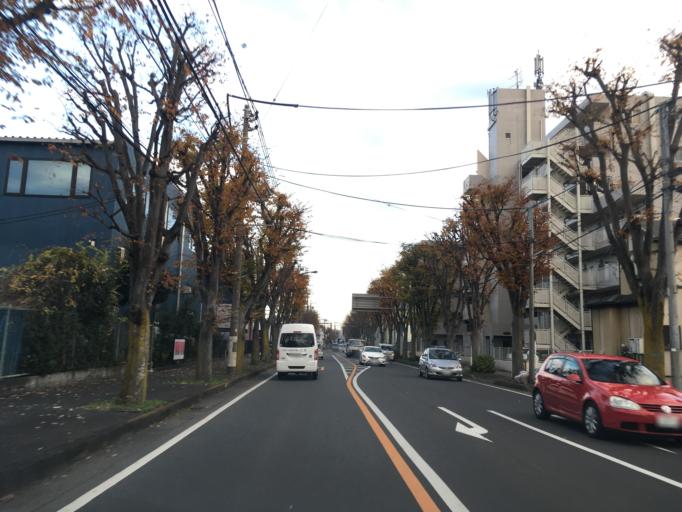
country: JP
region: Kanagawa
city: Zama
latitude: 35.5710
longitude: 139.3548
